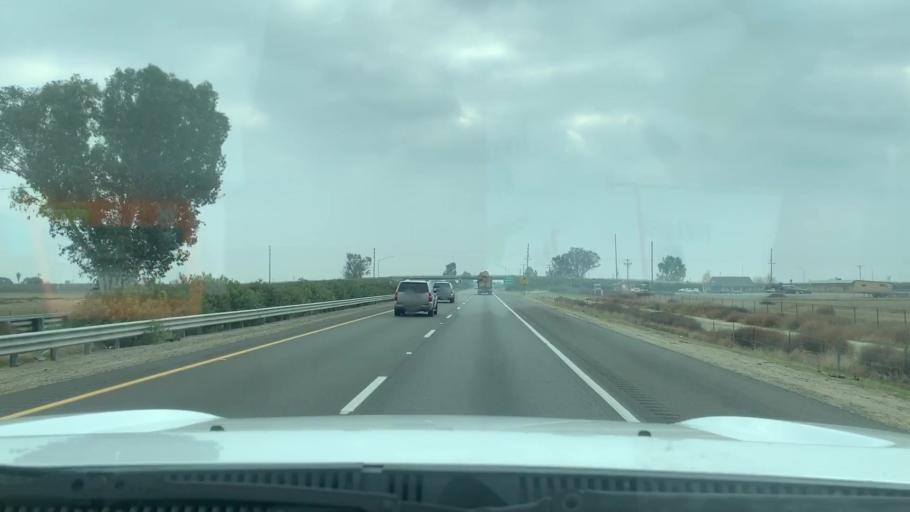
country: US
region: California
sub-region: Tulare County
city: Tipton
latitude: 36.1270
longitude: -119.3252
